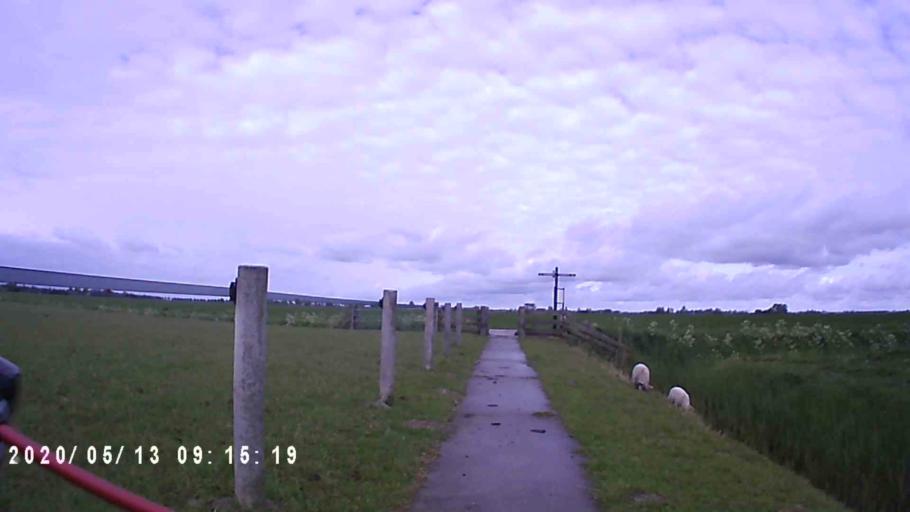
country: NL
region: Groningen
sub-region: Gemeente Zuidhorn
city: Noordhorn
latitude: 53.2737
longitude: 6.4133
